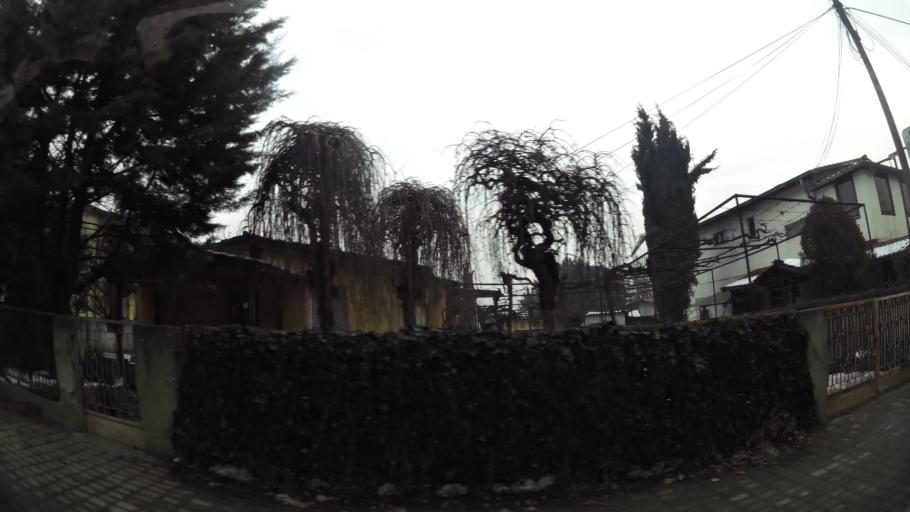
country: MK
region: Cair
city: Cair
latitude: 42.0131
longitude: 21.4579
